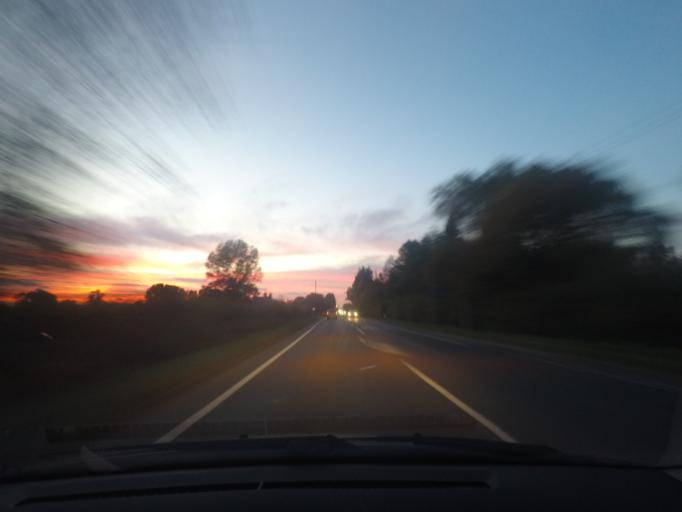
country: GB
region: England
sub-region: East Riding of Yorkshire
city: Thornton
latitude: 53.9306
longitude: -0.8265
